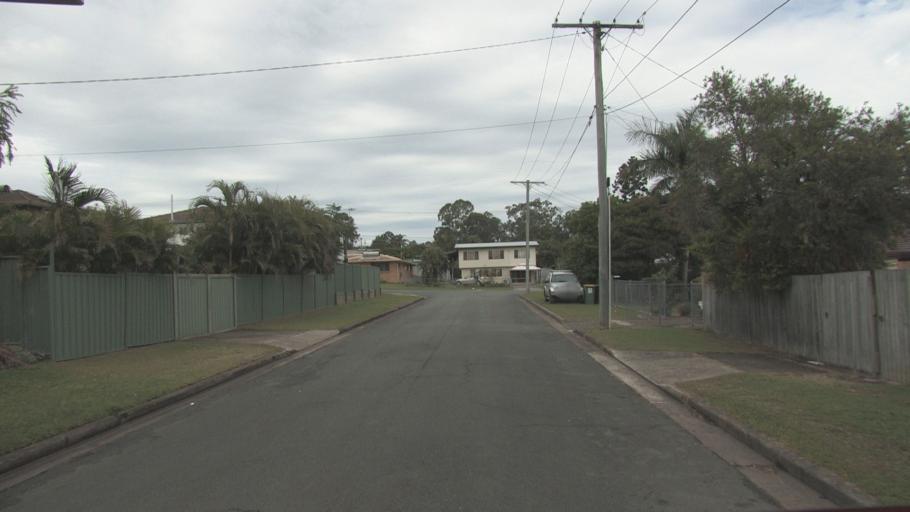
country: AU
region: Queensland
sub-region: Logan
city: Beenleigh
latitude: -27.7195
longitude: 153.1924
